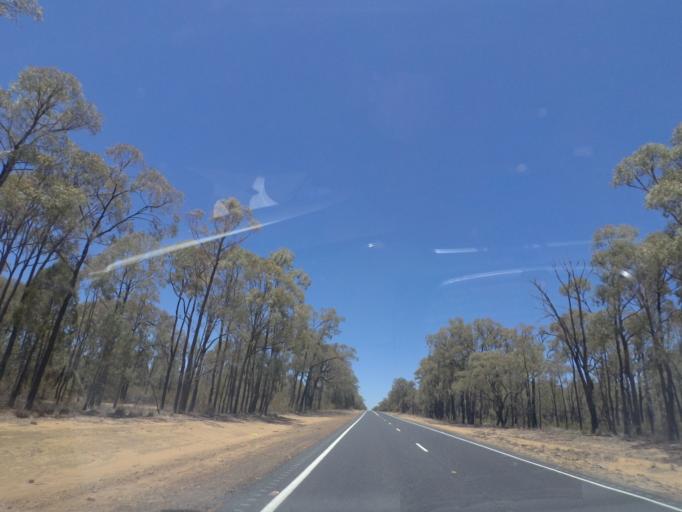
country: AU
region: New South Wales
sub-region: Narrabri
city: Narrabri
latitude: -30.7334
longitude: 149.5193
